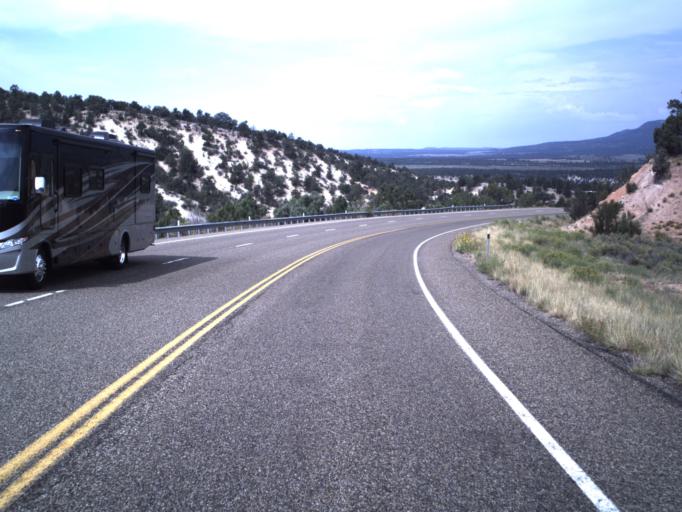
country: US
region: Utah
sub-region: Kane County
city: Kanab
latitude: 37.1961
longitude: -112.6645
